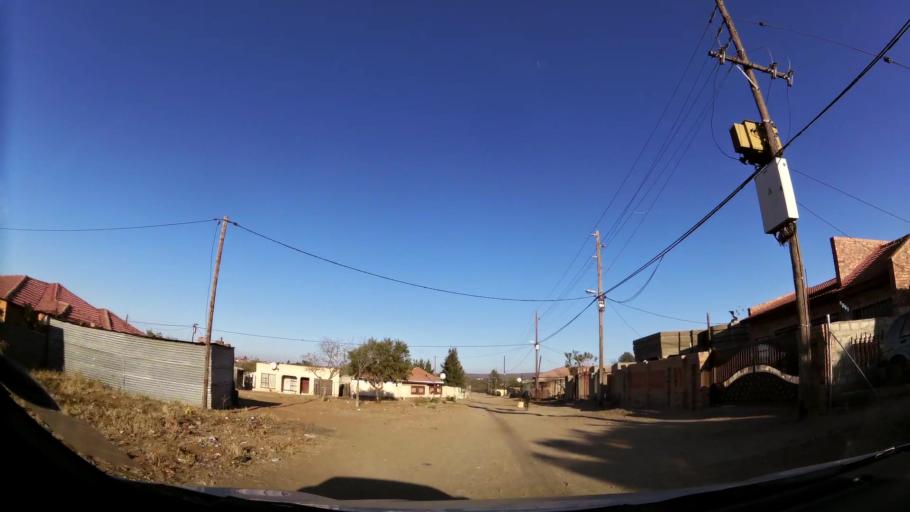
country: ZA
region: Limpopo
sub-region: Capricorn District Municipality
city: Polokwane
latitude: -23.8399
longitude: 29.3622
